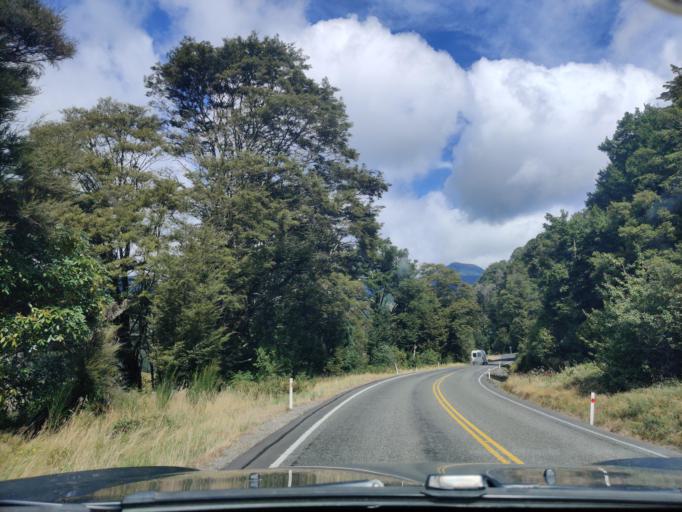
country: NZ
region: Tasman
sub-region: Tasman District
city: Wakefield
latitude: -41.7070
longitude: 172.5842
